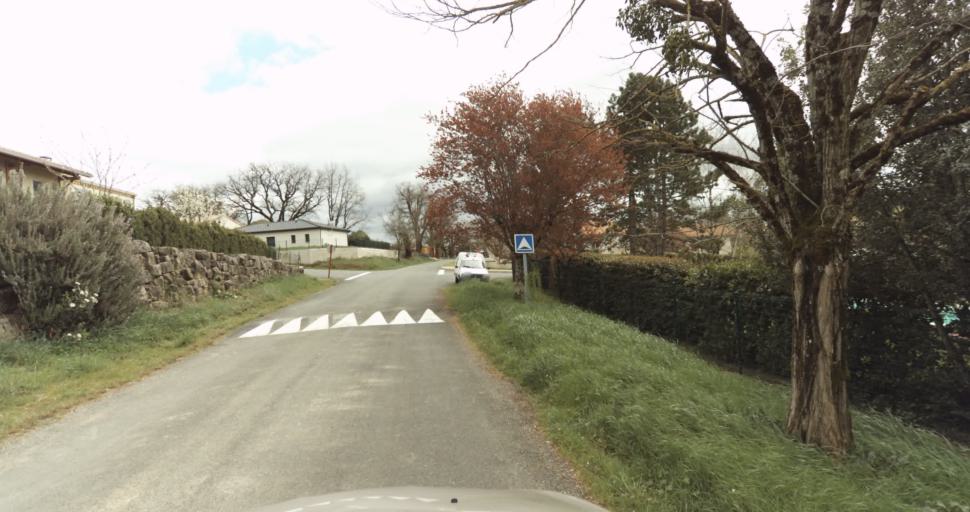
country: FR
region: Midi-Pyrenees
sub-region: Departement du Tarn
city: Puygouzon
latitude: 43.8968
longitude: 2.1765
